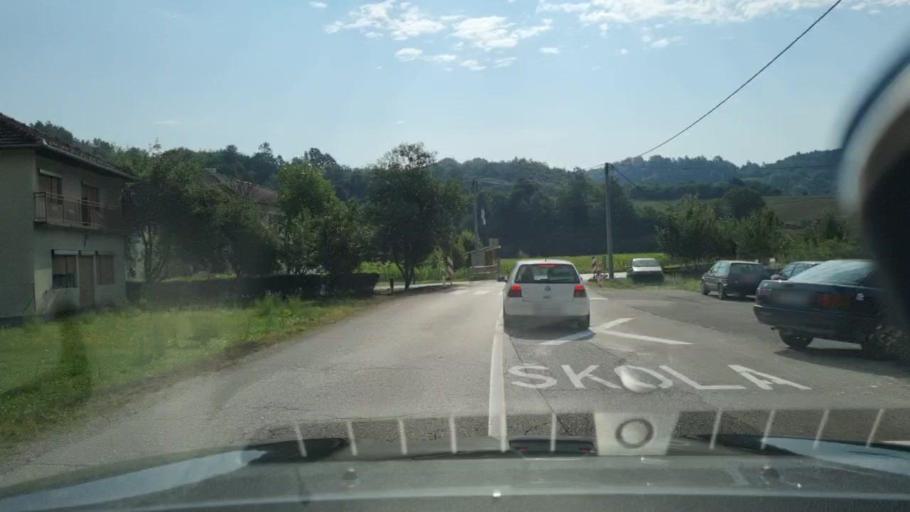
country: BA
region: Federation of Bosnia and Herzegovina
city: Otoka
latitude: 44.9964
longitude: 16.1546
